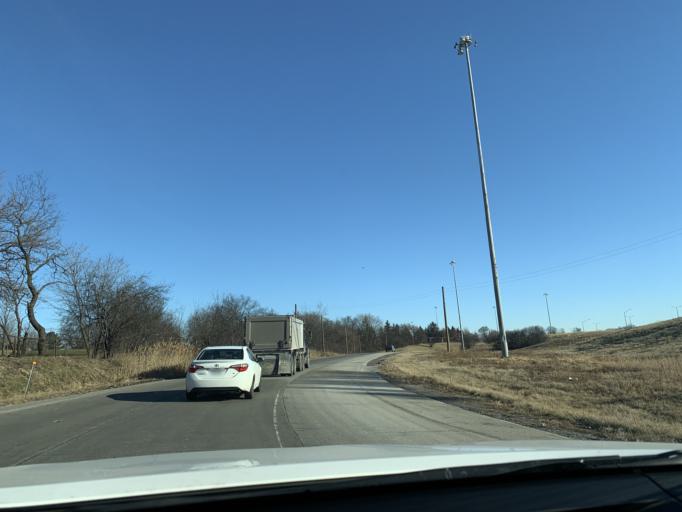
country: US
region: Illinois
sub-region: Cook County
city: Indian Head Park
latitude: 41.7629
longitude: -87.8942
